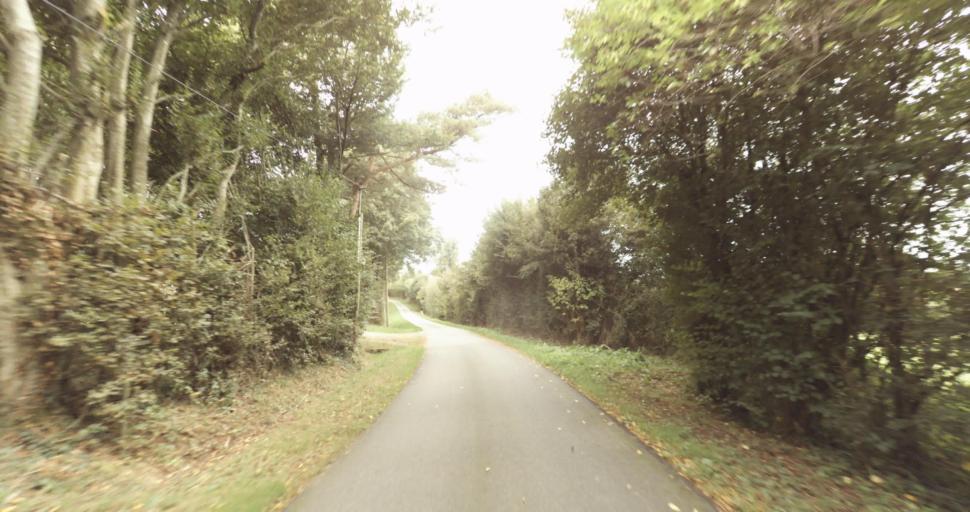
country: FR
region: Lower Normandy
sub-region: Departement de l'Orne
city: Gace
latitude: 48.7503
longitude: 0.3069
